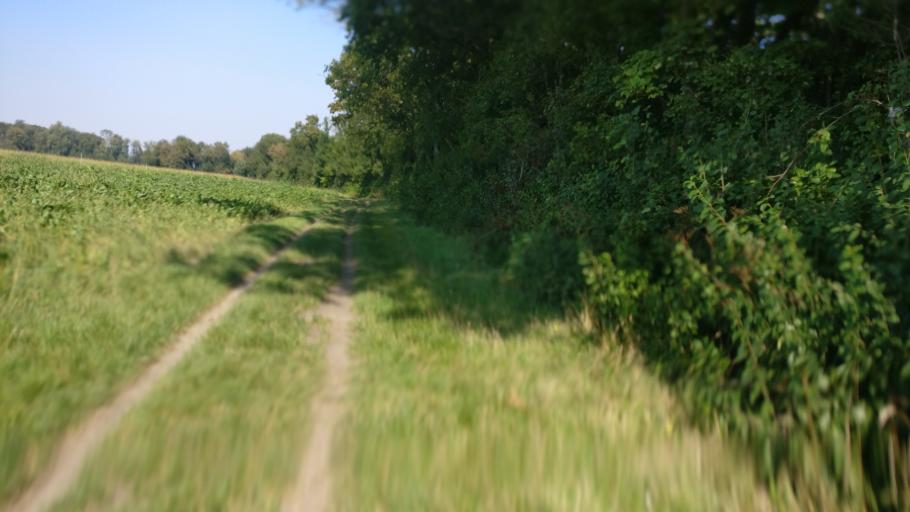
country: AT
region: Lower Austria
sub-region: Politischer Bezirk Baden
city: Mitterndorf an der Fischa
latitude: 47.9681
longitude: 16.4380
